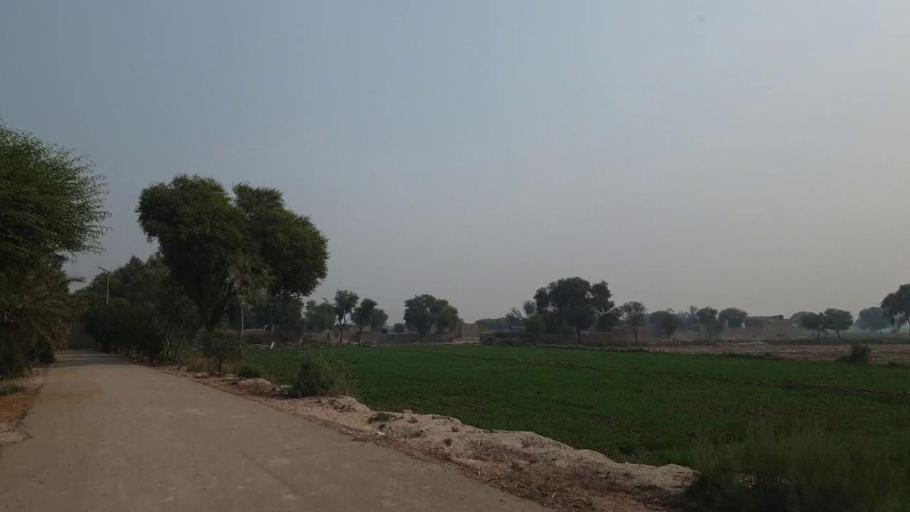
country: PK
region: Sindh
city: Bhan
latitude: 26.5258
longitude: 67.7245
